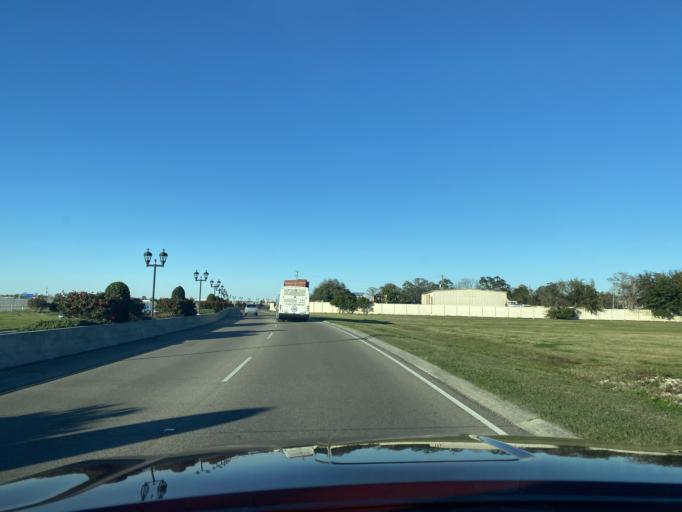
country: US
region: Louisiana
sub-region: Jefferson Parish
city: Kenner
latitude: 29.9890
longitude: -90.2478
